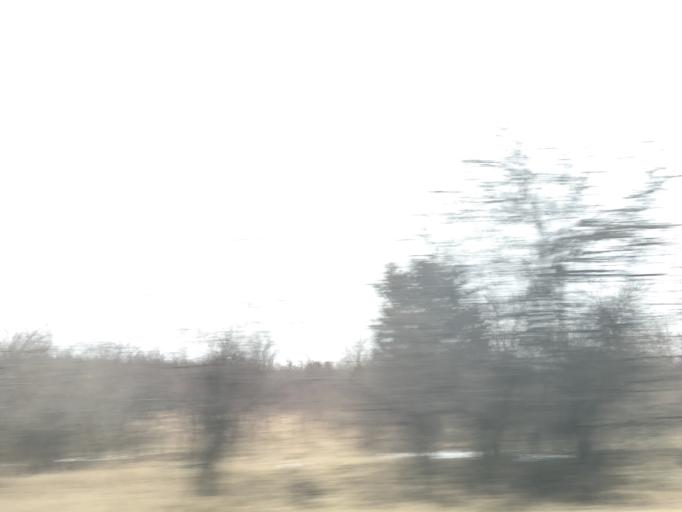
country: US
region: Illinois
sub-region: Cook County
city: Streamwood
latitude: 42.0610
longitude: -88.1673
